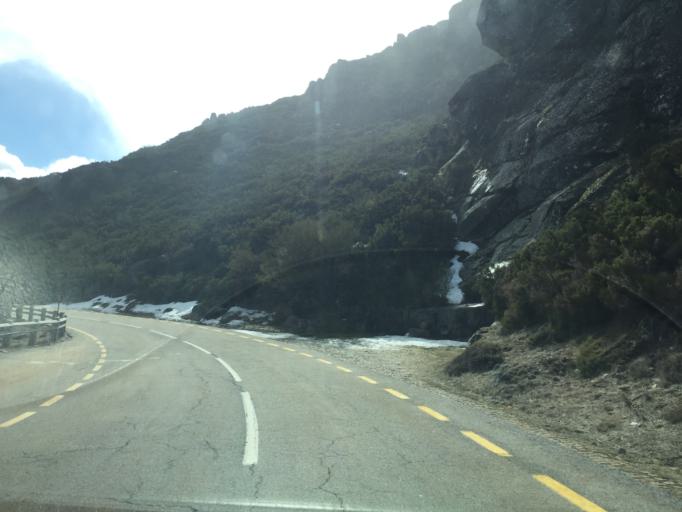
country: PT
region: Castelo Branco
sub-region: Covilha
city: Covilha
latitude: 40.3207
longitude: -7.5889
